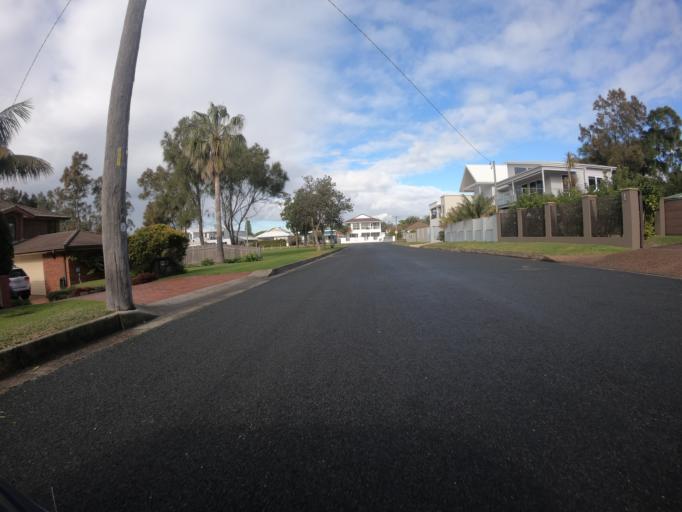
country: AU
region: New South Wales
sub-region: Wollongong
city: East Corrimal
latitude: -34.3757
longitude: 150.9184
